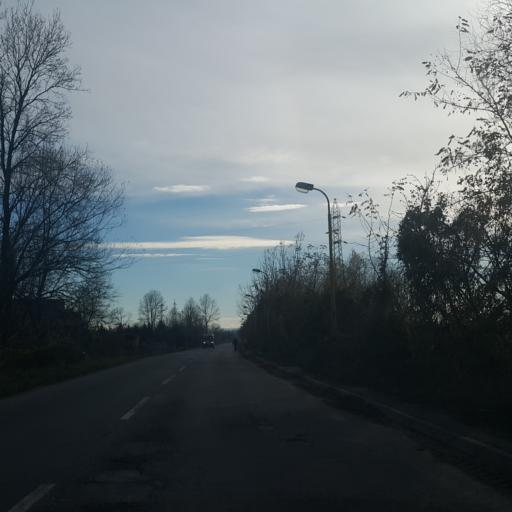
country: RS
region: Central Serbia
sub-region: Belgrade
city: Lazarevac
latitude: 44.4275
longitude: 20.2790
